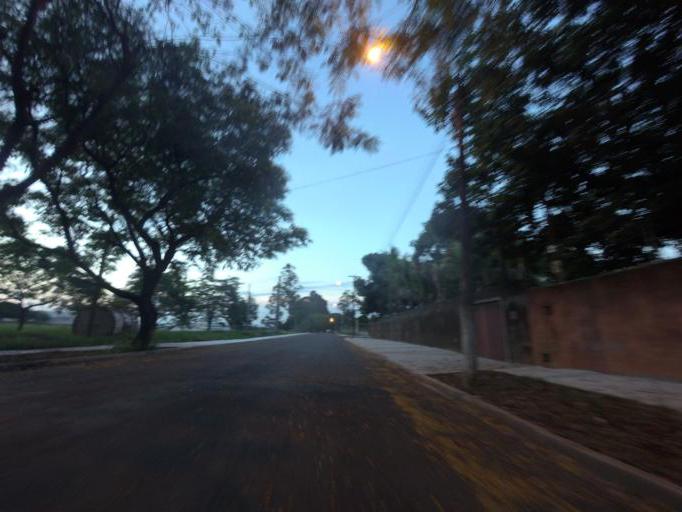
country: BR
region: Sao Paulo
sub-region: Piracicaba
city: Piracicaba
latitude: -22.7601
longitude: -47.5960
